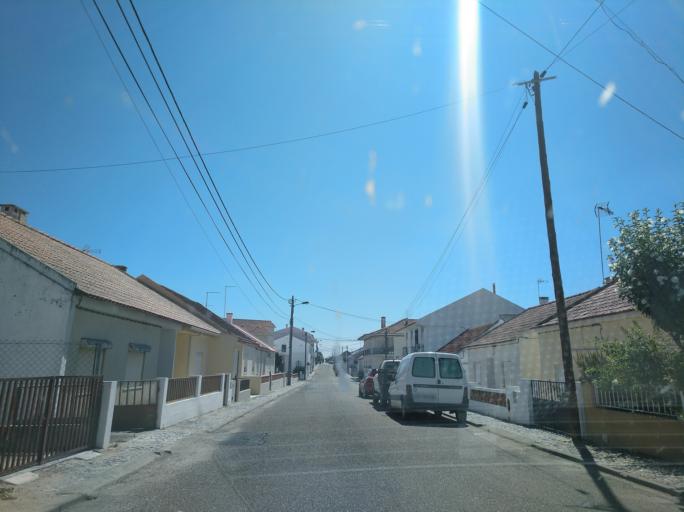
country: PT
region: Evora
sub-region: Vendas Novas
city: Vendas Novas
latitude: 38.6802
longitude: -8.4709
